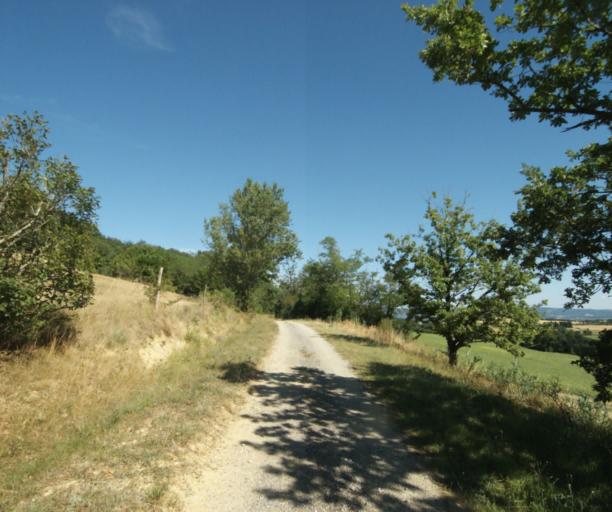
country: FR
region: Midi-Pyrenees
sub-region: Departement de la Haute-Garonne
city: Saint-Felix-Lauragais
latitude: 43.5158
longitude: 1.9196
